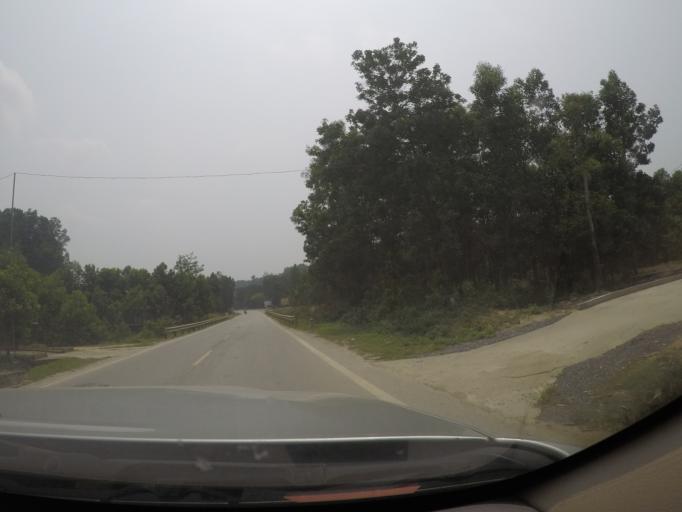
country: VN
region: Thanh Hoa
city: Thi Tran Thuong Xuan
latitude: 19.7933
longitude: 105.3993
